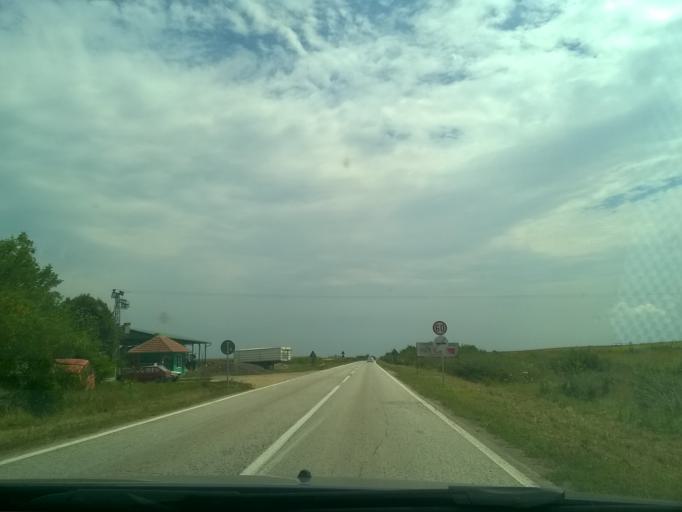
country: RS
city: Banatski Despotovac
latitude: 45.3853
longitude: 20.6357
